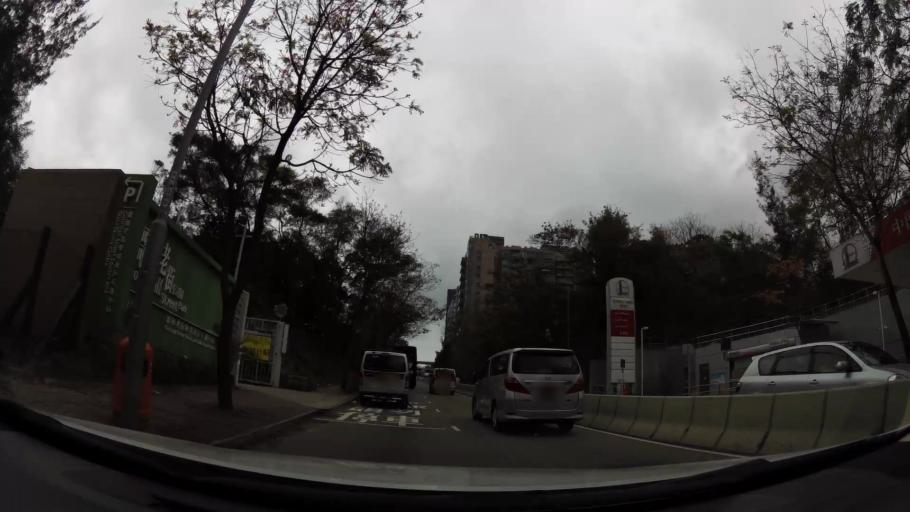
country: HK
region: Wong Tai Sin
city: Wong Tai Sin
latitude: 22.3400
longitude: 114.1737
